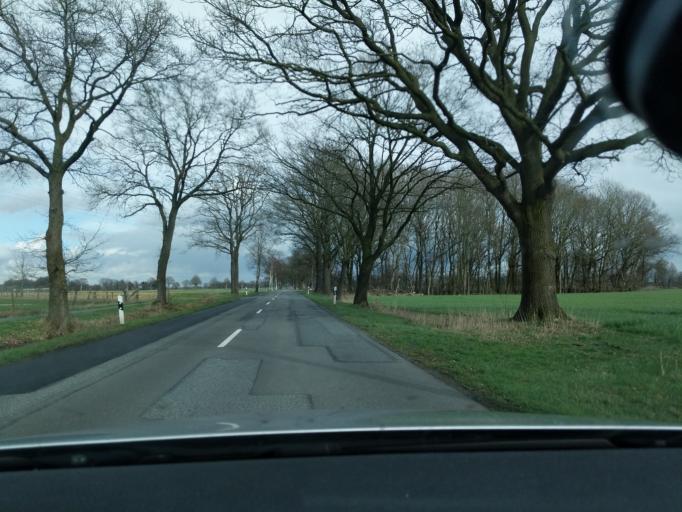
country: DE
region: Lower Saxony
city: Estorf
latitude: 53.5840
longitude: 9.2158
